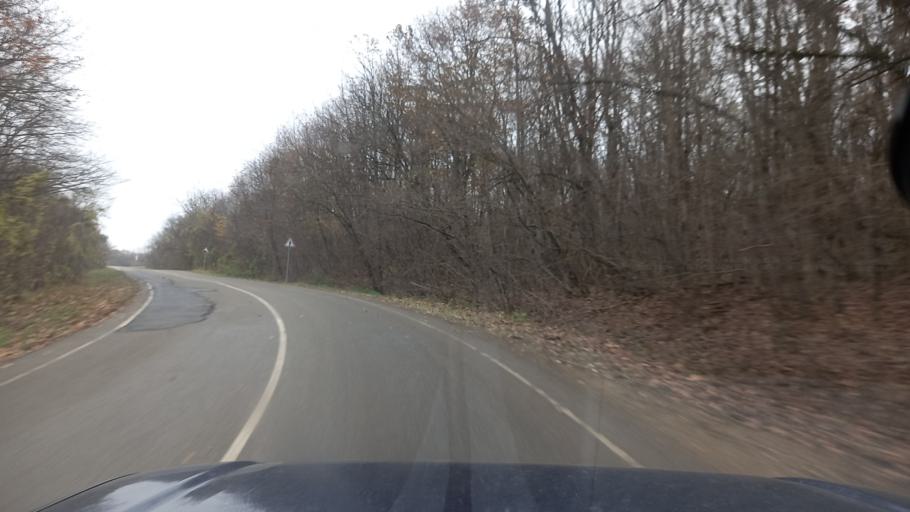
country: RU
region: Krasnodarskiy
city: Goryachiy Klyuch
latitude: 44.5419
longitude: 39.2569
